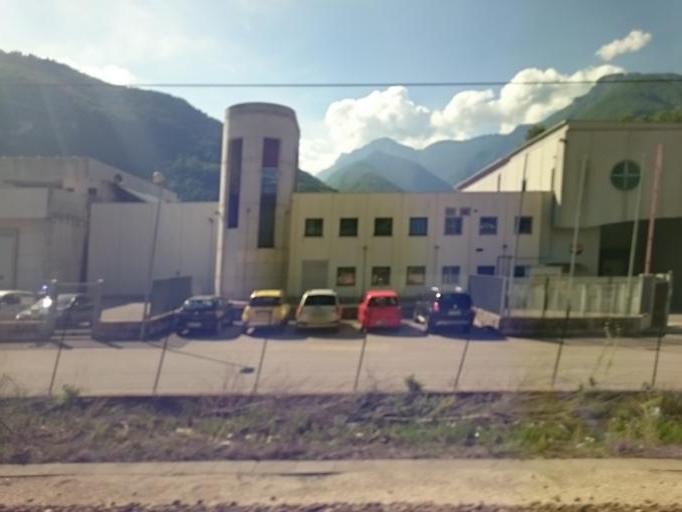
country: IT
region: Trentino-Alto Adige
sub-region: Provincia di Trento
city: Ala
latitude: 45.7672
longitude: 11.0055
